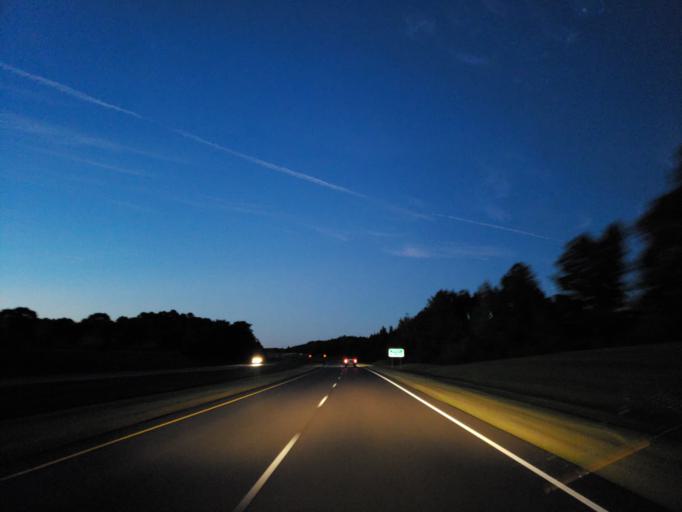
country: US
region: Mississippi
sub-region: Clarke County
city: Quitman
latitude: 32.0467
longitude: -88.6766
